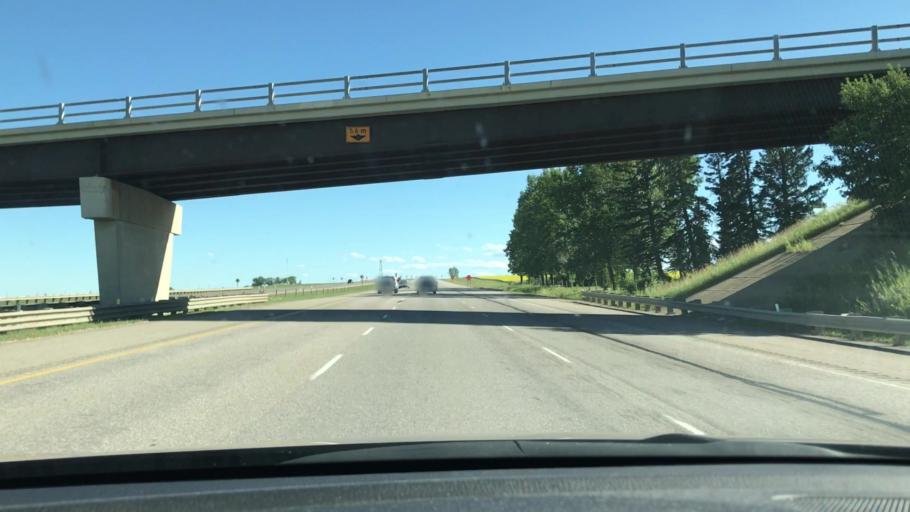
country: CA
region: Alberta
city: Crossfield
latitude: 51.4315
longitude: -114.0020
